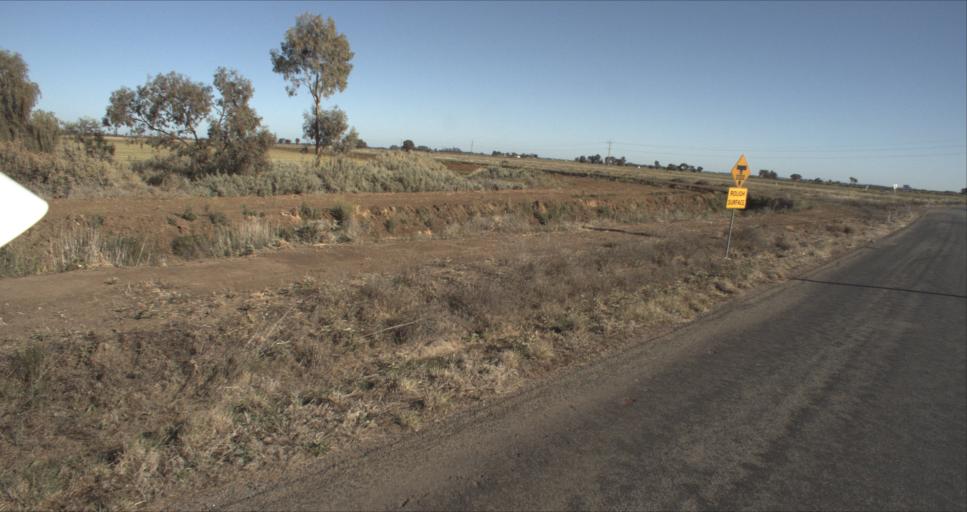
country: AU
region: New South Wales
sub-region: Leeton
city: Leeton
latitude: -34.5510
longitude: 146.2673
